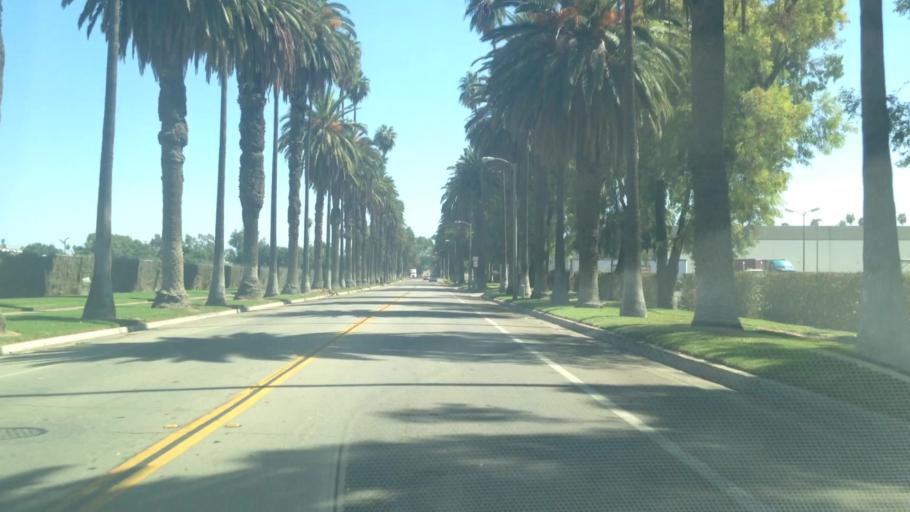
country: US
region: California
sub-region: Riverside County
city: Riverside
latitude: 33.9274
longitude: -117.4089
